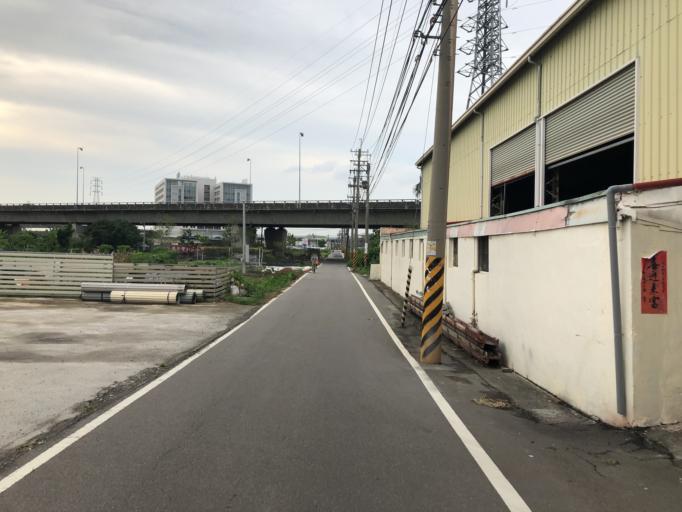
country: TW
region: Taiwan
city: Zhongxing New Village
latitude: 24.0506
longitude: 120.6890
